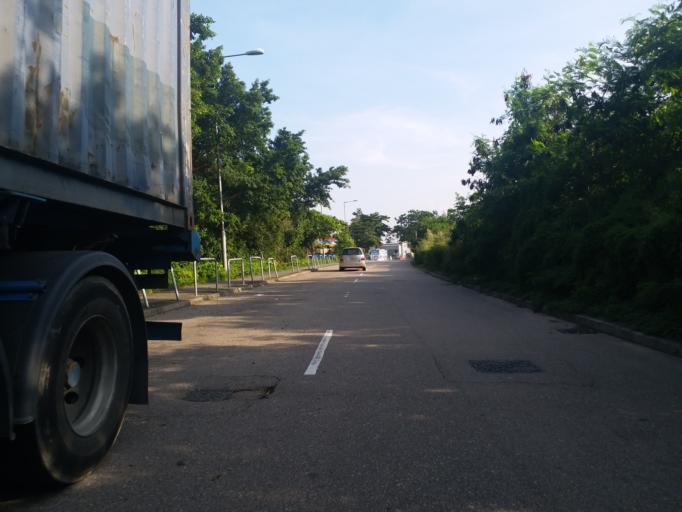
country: HK
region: Yuen Long
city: Yuen Long Kau Hui
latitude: 22.4744
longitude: 114.0515
